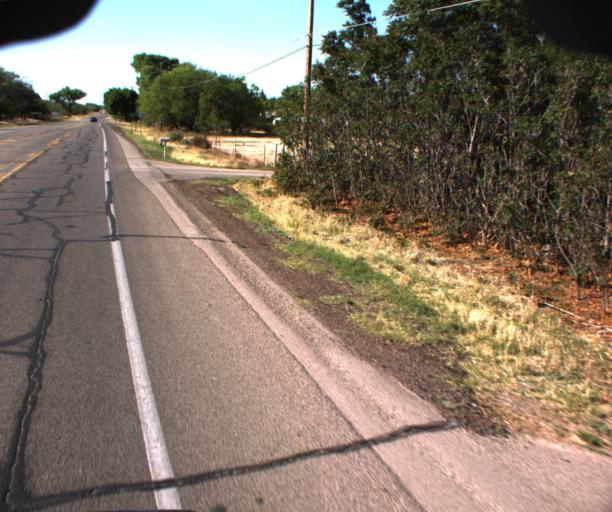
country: US
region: Arizona
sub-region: Cochise County
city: Saint David
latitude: 31.9025
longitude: -110.2136
